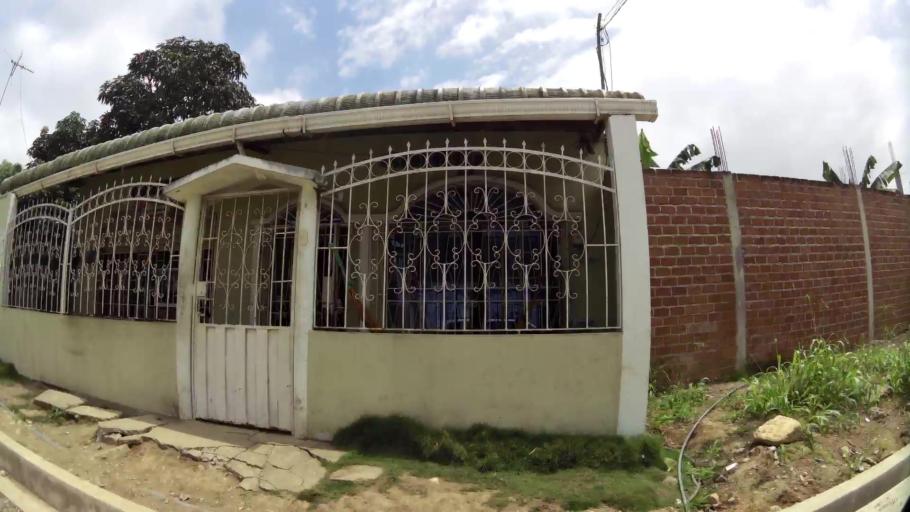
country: EC
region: El Oro
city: Pasaje
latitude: -3.2379
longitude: -79.8257
